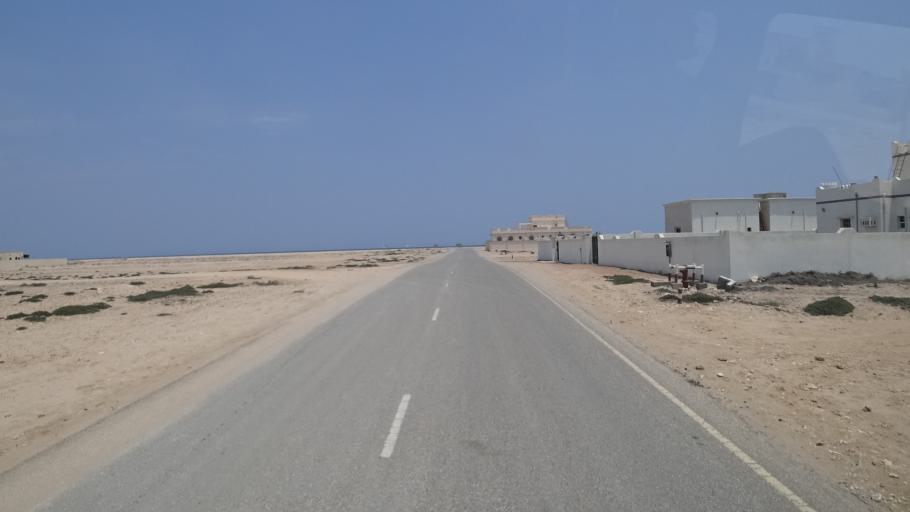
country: OM
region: Ash Sharqiyah
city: Sur
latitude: 22.5271
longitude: 59.7947
